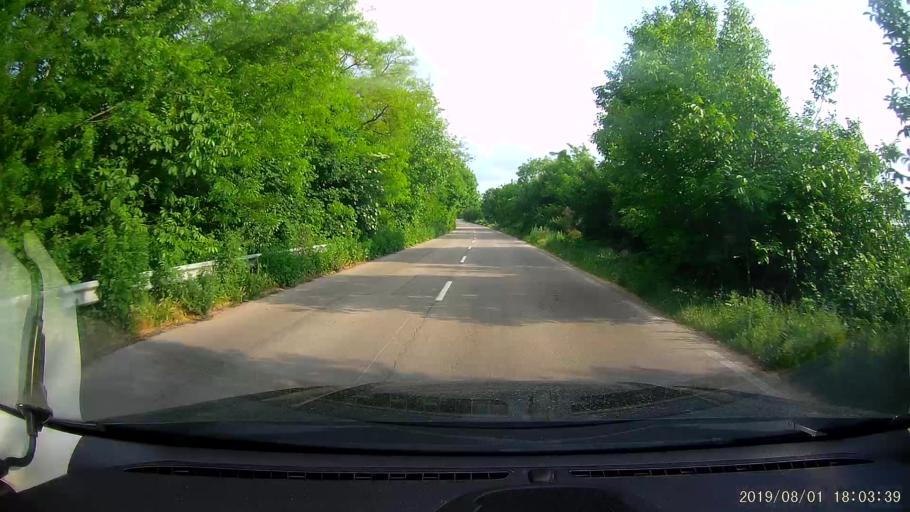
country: BG
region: Silistra
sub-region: Obshtina Alfatar
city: Alfatar
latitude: 43.9226
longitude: 27.2890
